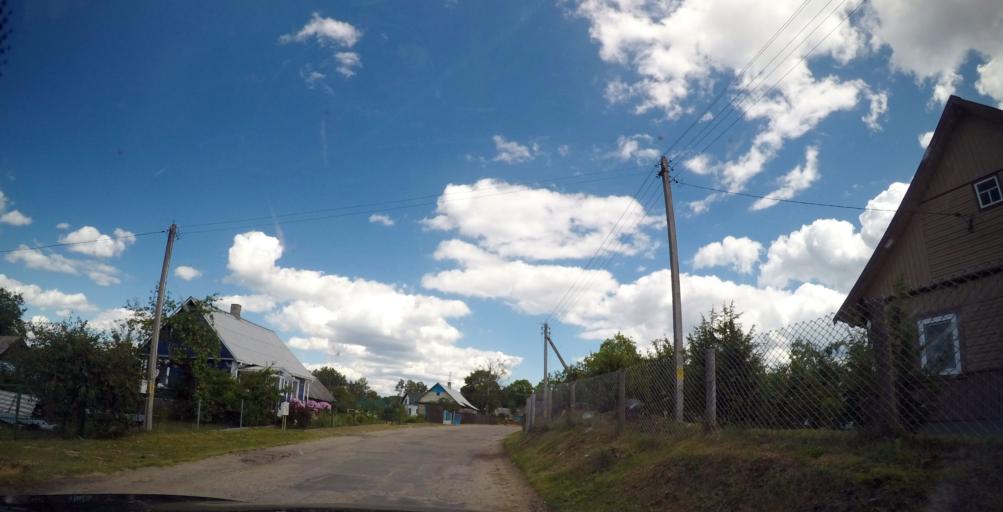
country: BY
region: Grodnenskaya
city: Skidal'
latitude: 53.8205
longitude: 24.2465
